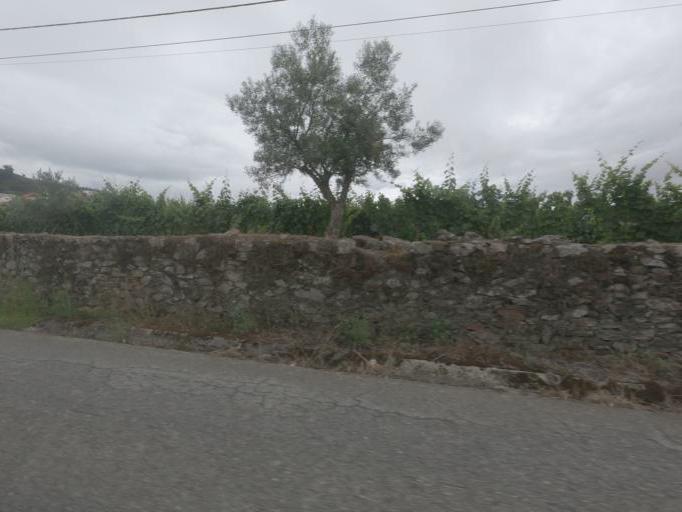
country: PT
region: Vila Real
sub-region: Sabrosa
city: Sabrosa
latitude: 41.2909
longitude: -7.5245
